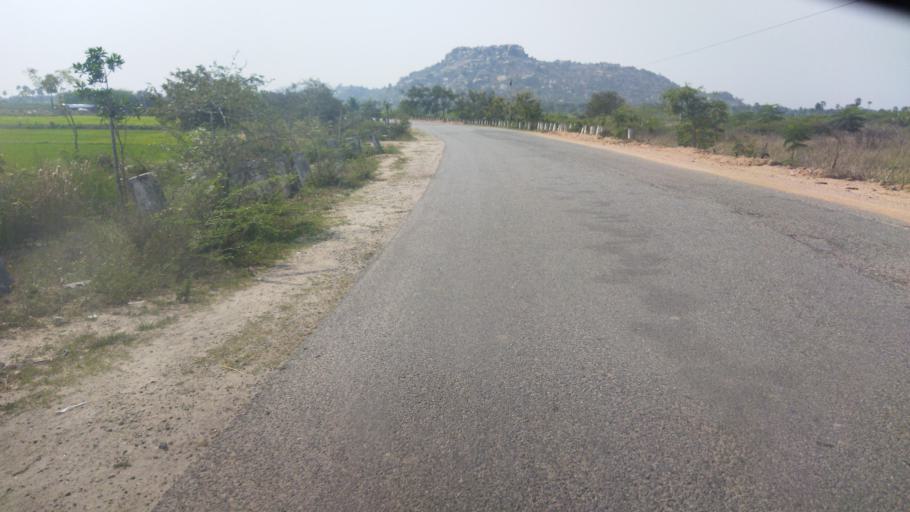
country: IN
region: Telangana
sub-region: Nalgonda
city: Nalgonda
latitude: 17.1113
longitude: 79.2793
